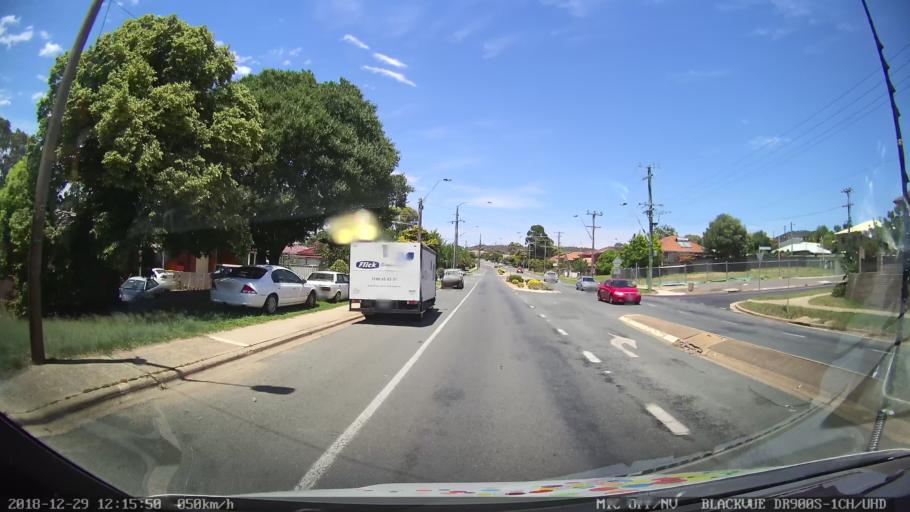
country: AU
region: New South Wales
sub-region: Queanbeyan
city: Queanbeyan
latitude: -35.3649
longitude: 149.2340
